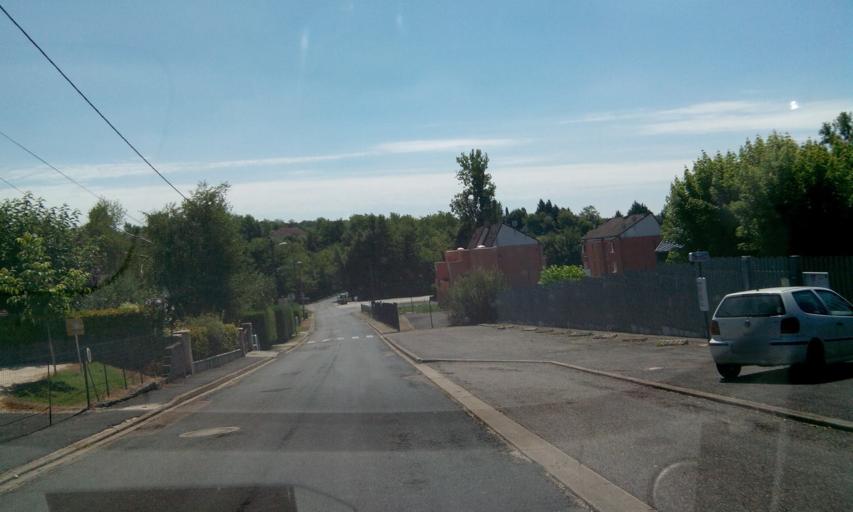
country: FR
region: Limousin
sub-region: Departement de la Correze
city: Meyssac
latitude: 45.0512
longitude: 1.6743
